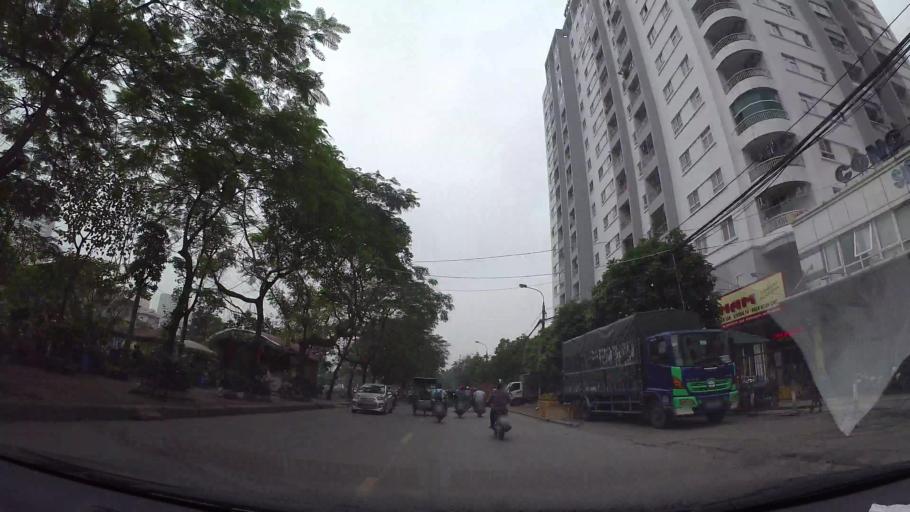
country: VN
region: Ha Noi
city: Hai BaTrung
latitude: 20.9936
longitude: 105.8623
